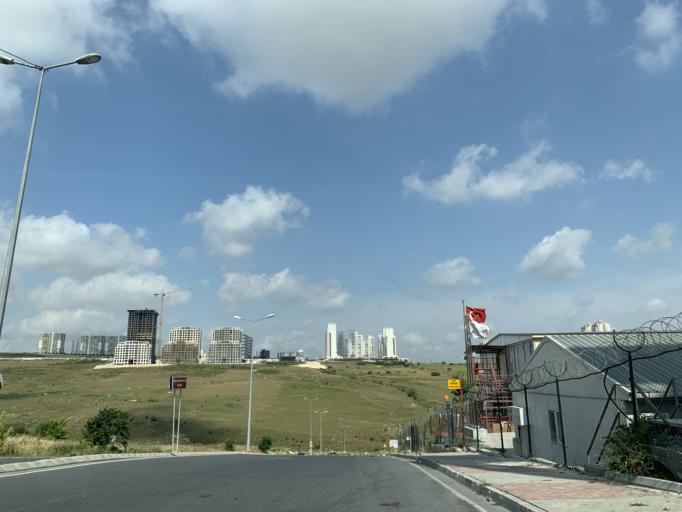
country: TR
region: Istanbul
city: Esenyurt
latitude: 41.0695
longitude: 28.7007
